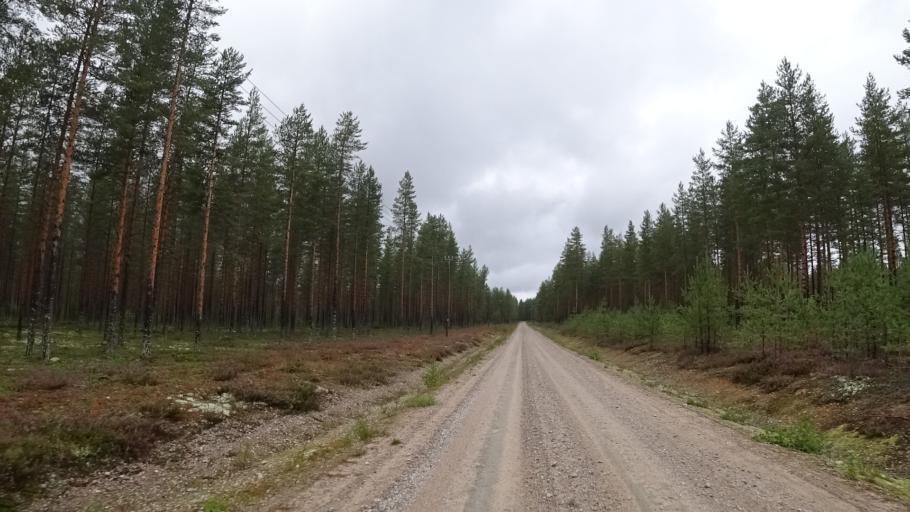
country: FI
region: North Karelia
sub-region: Pielisen Karjala
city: Lieksa
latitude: 63.5366
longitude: 30.0484
